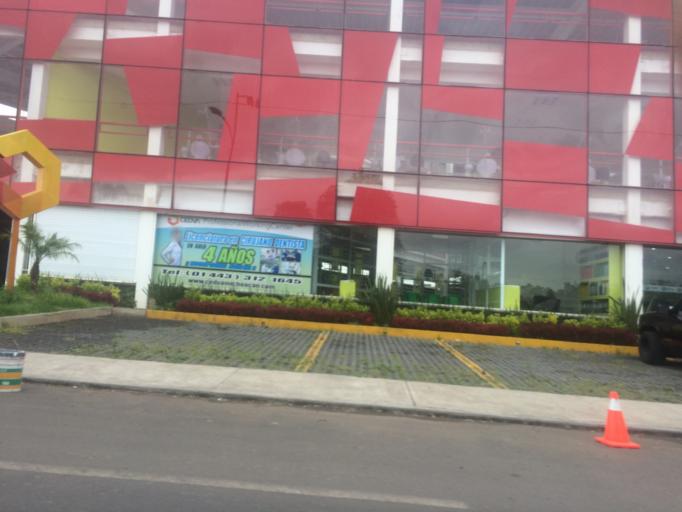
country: MX
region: Michoacan
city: Morelia
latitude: 19.7179
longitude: -101.1797
